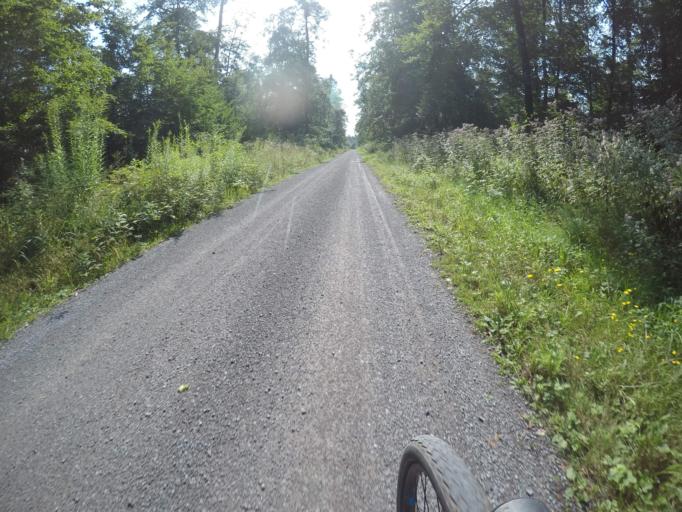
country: DE
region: Baden-Wuerttemberg
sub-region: Karlsruhe Region
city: Hockenheim
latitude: 49.3349
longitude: 8.5780
